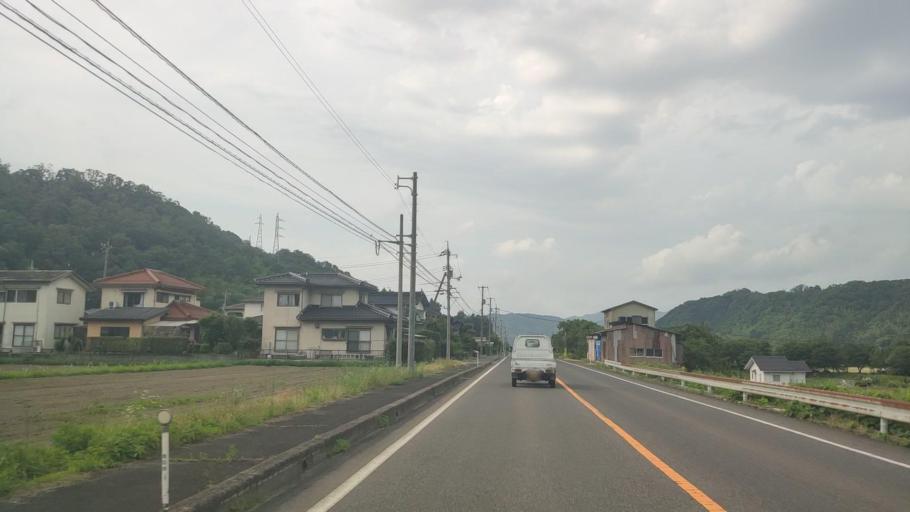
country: JP
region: Tottori
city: Kurayoshi
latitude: 35.3859
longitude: 133.8562
